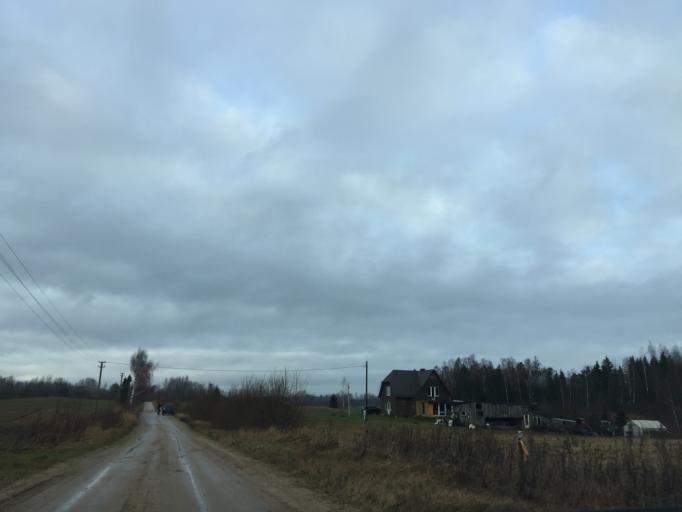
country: LV
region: Vainode
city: Vainode
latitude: 56.6072
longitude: 21.7990
